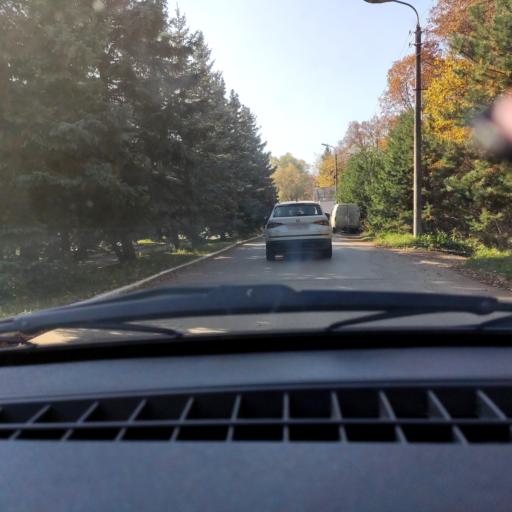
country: RU
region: Bashkortostan
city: Mikhaylovka
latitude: 54.8046
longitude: 55.8622
